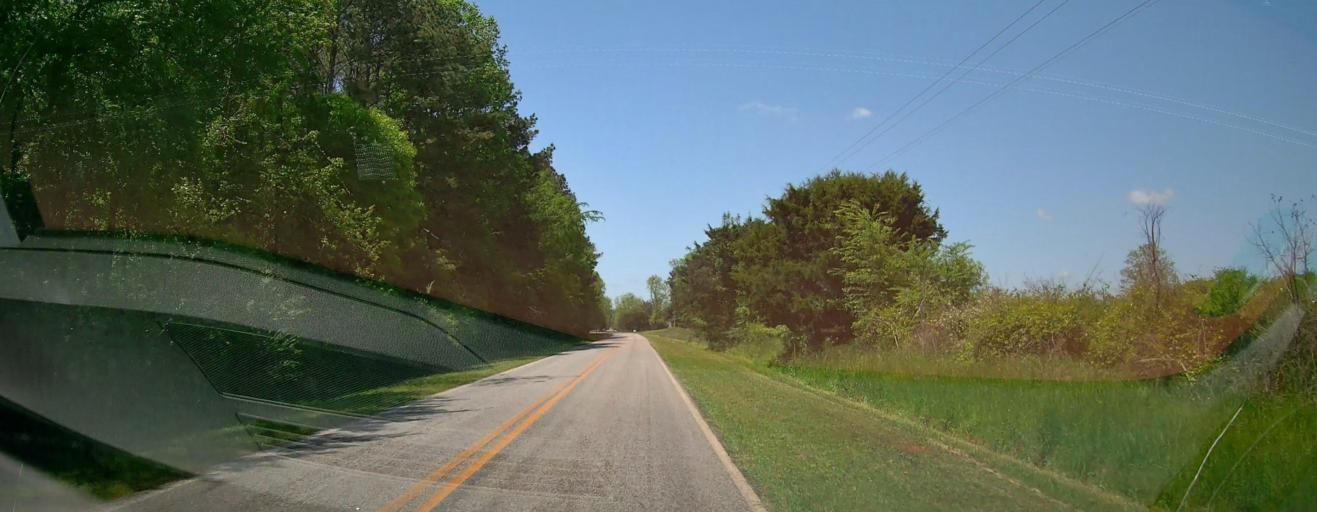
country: US
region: Georgia
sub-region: Jasper County
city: Monticello
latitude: 33.2776
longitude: -83.6679
